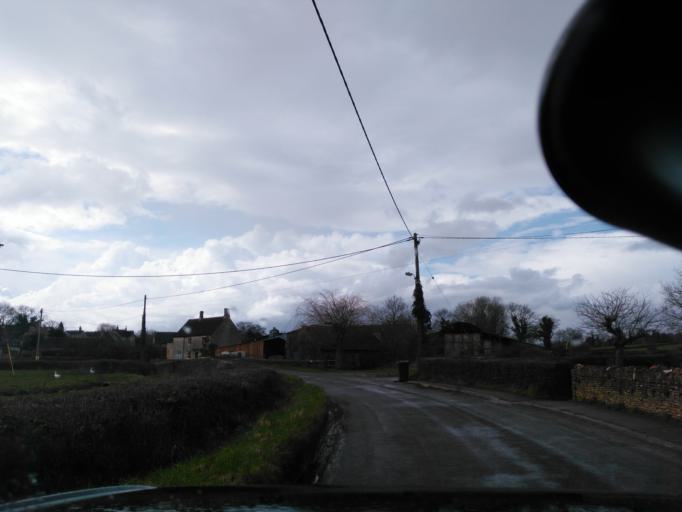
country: GB
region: England
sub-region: Wiltshire
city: Atworth
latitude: 51.3949
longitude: -2.1821
